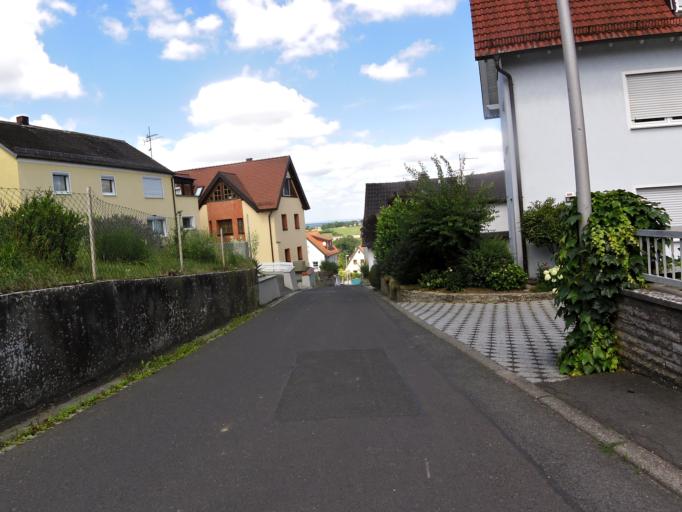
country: DE
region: Bavaria
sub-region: Regierungsbezirk Unterfranken
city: Kist
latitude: 49.7432
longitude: 9.8392
